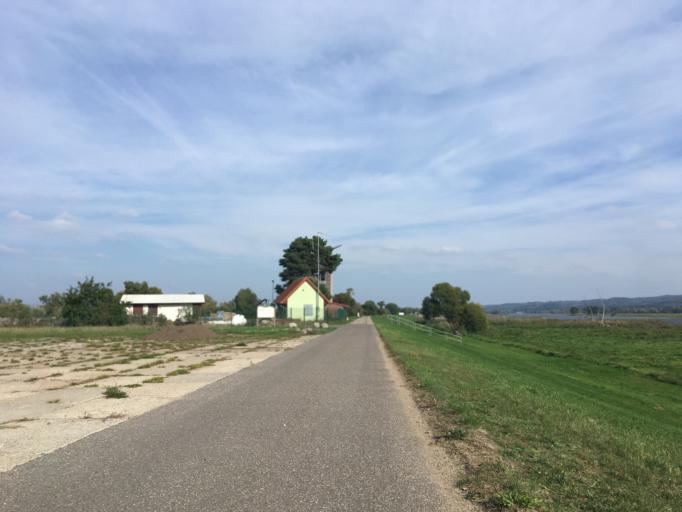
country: DE
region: Brandenburg
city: Schoneberg
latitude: 52.9824
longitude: 14.1914
